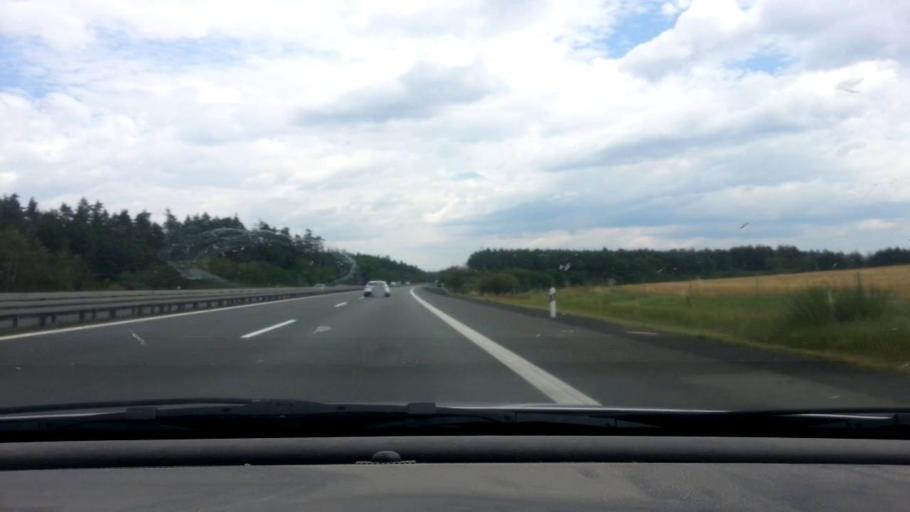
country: DE
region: Bavaria
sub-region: Upper Palatinate
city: Wiesau
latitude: 49.8744
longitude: 12.1930
